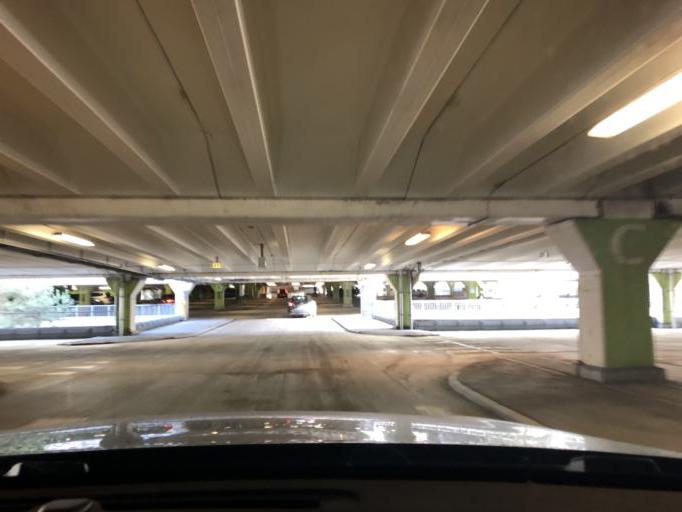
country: SE
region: Stockholm
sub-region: Huddinge Kommun
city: Segeltorp
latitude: 59.2748
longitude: 17.9102
